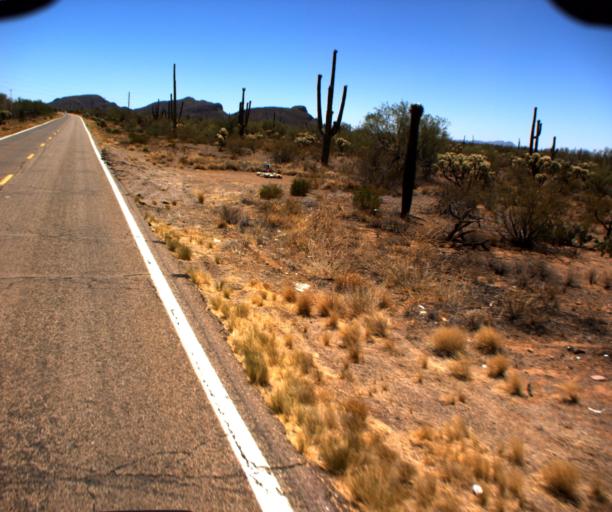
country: US
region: Arizona
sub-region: Pima County
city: Sells
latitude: 31.9879
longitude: -111.9756
